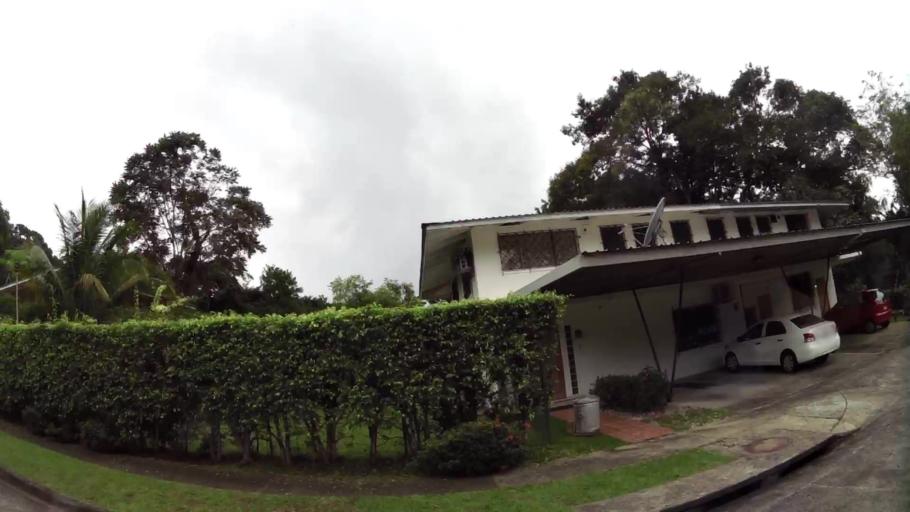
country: PA
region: Panama
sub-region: Distrito de Panama
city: Ancon
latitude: 8.9533
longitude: -79.5543
